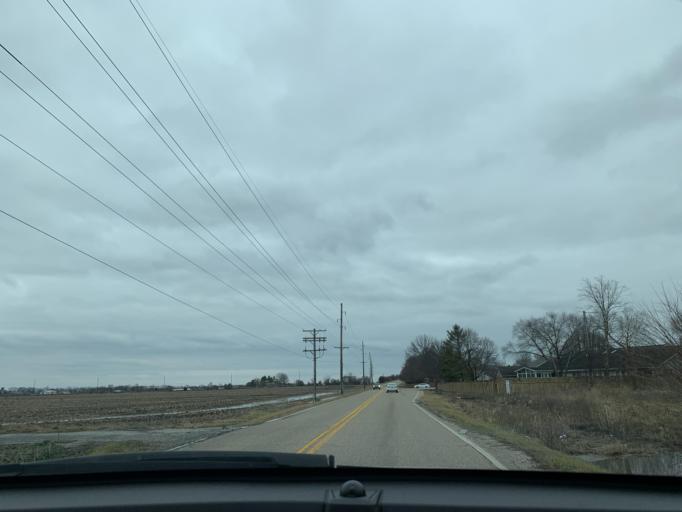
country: US
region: Illinois
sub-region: Sangamon County
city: Jerome
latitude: 39.7498
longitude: -89.6867
